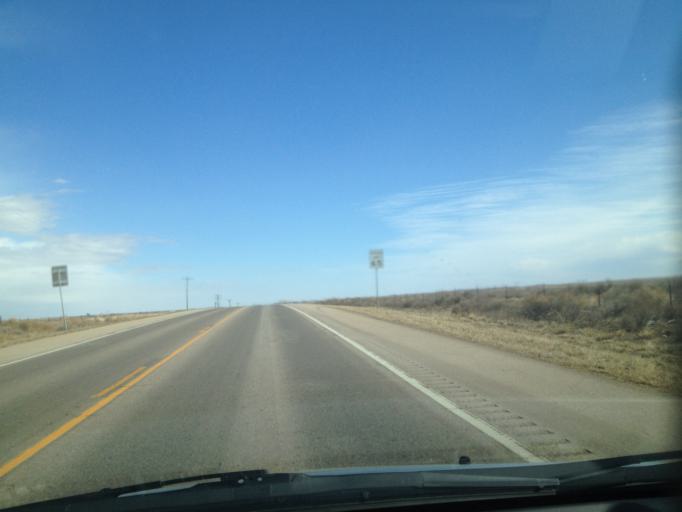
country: US
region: Colorado
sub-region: Weld County
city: Kersey
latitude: 40.2939
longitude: -104.3042
